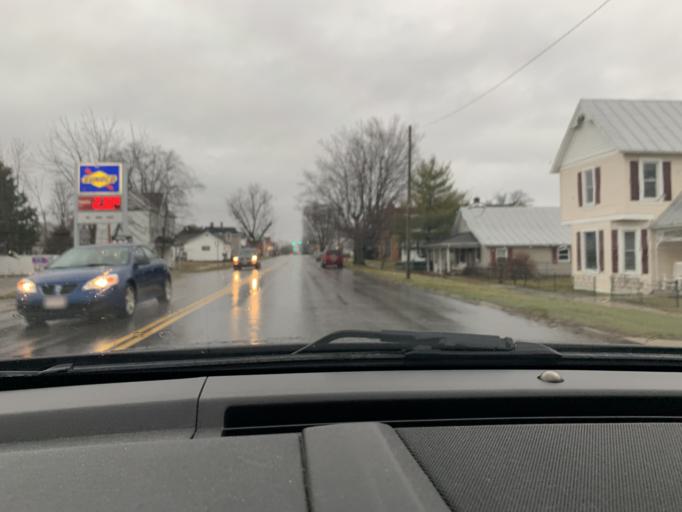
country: US
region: Ohio
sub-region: Ross County
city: Kingston
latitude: 39.4712
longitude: -82.9119
